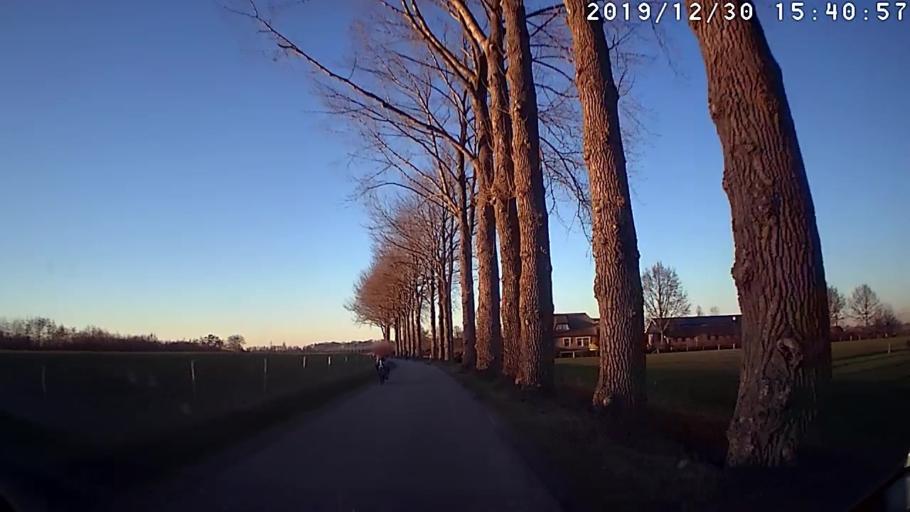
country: NL
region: Overijssel
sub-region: Gemeente Zwolle
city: Zwolle
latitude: 52.4664
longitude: 6.1462
